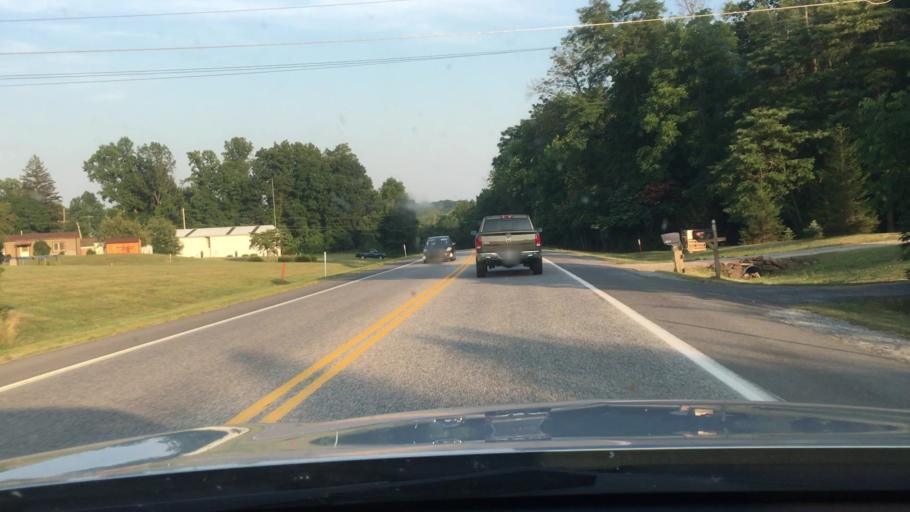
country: US
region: Pennsylvania
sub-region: York County
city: Dillsburg
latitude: 40.0848
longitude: -76.9424
